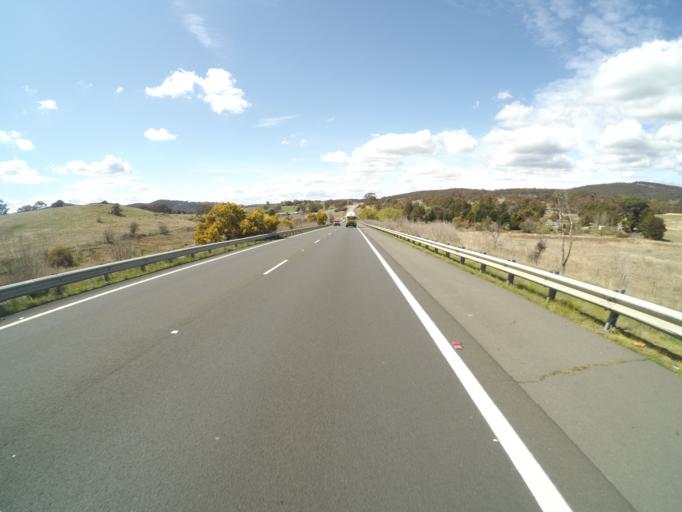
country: AU
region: New South Wales
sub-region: Goulburn Mulwaree
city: Goulburn
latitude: -34.7333
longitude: 149.8042
